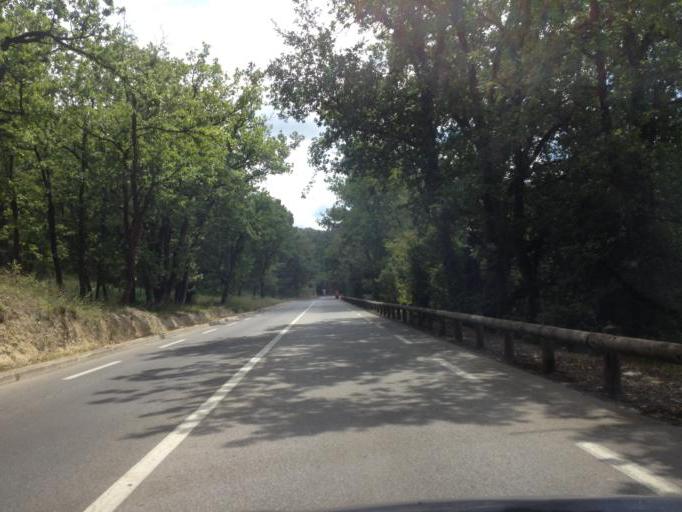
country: FR
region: Provence-Alpes-Cote d'Azur
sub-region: Departement du Vaucluse
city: Vaison-la-Romaine
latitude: 44.2421
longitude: 5.0503
